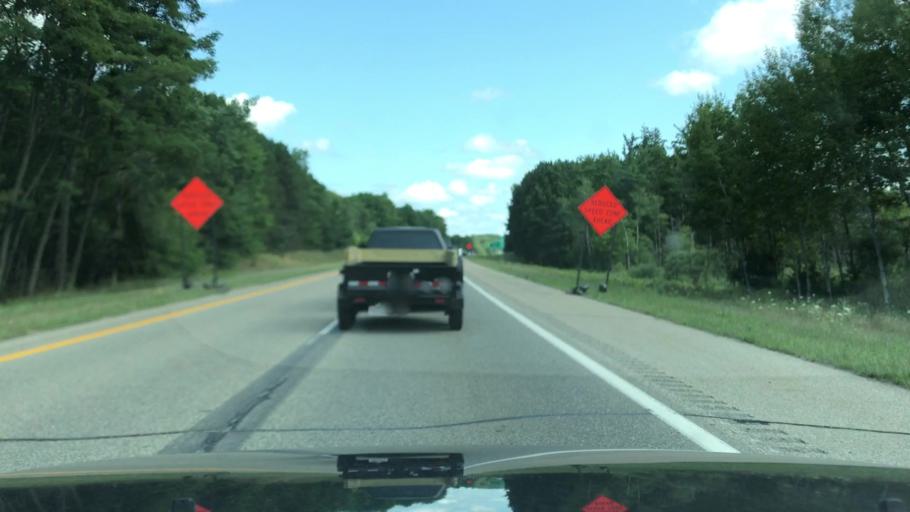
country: US
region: Michigan
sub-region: Mecosta County
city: Big Rapids
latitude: 43.7321
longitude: -85.5328
